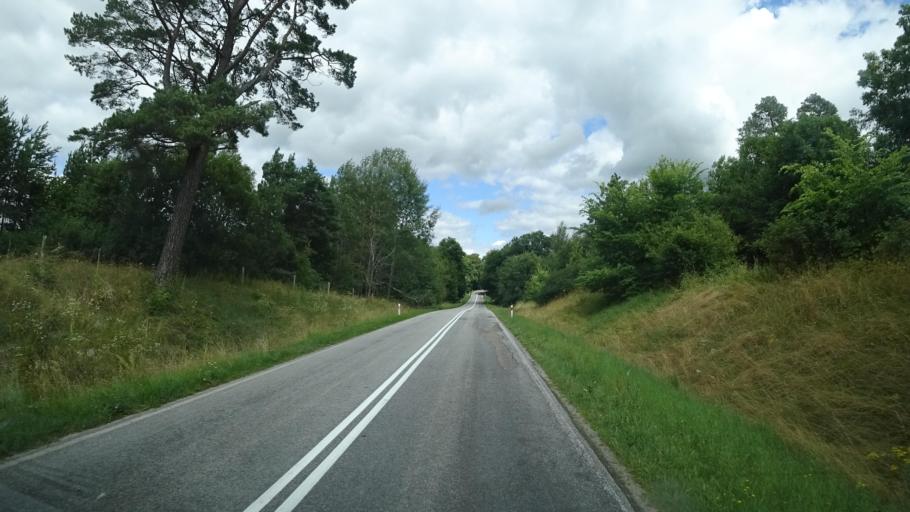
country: PL
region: Warmian-Masurian Voivodeship
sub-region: Powiat goldapski
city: Goldap
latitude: 54.2090
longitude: 22.2019
